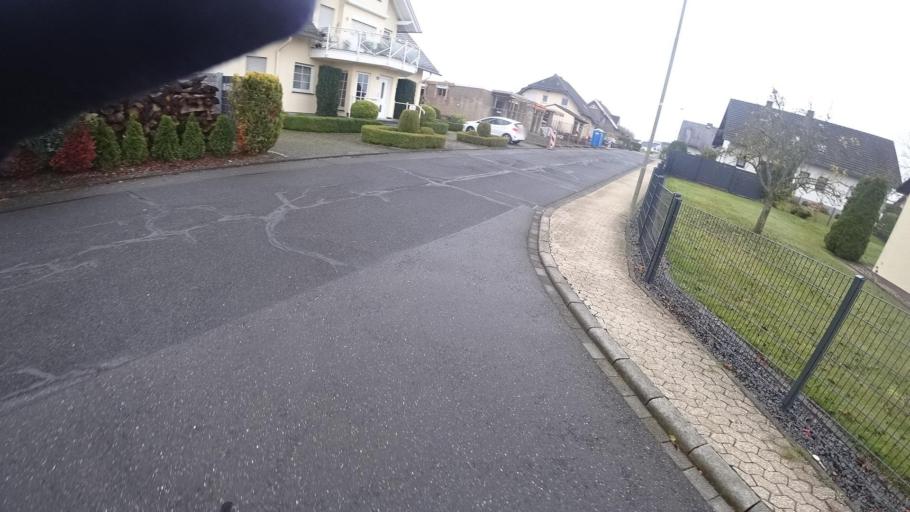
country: DE
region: Rheinland-Pfalz
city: Halsenbach
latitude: 50.1744
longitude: 7.5561
